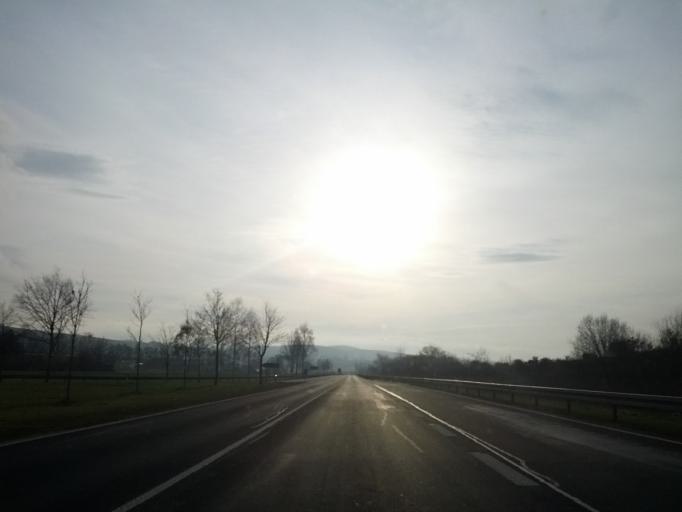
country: DE
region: Thuringia
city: Fambach
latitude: 50.7414
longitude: 10.3572
